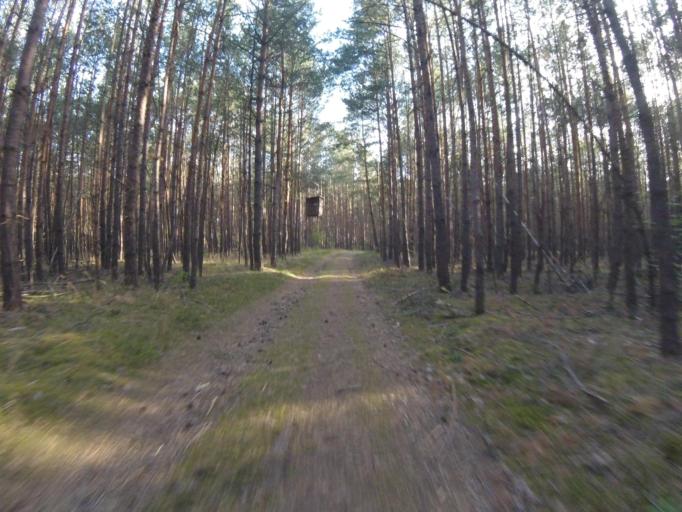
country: DE
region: Brandenburg
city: Wildau
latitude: 52.3349
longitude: 13.6764
